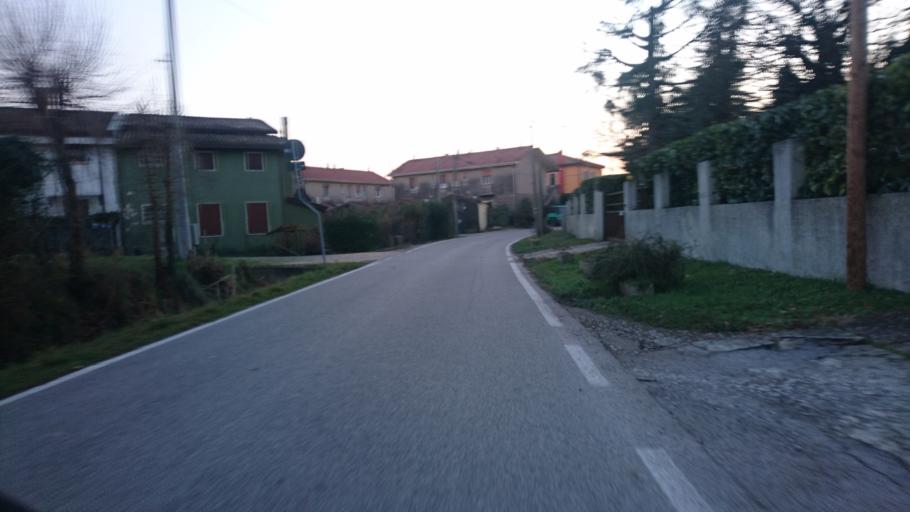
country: IT
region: Veneto
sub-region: Provincia di Padova
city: Legnaro
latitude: 45.3575
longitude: 11.9628
